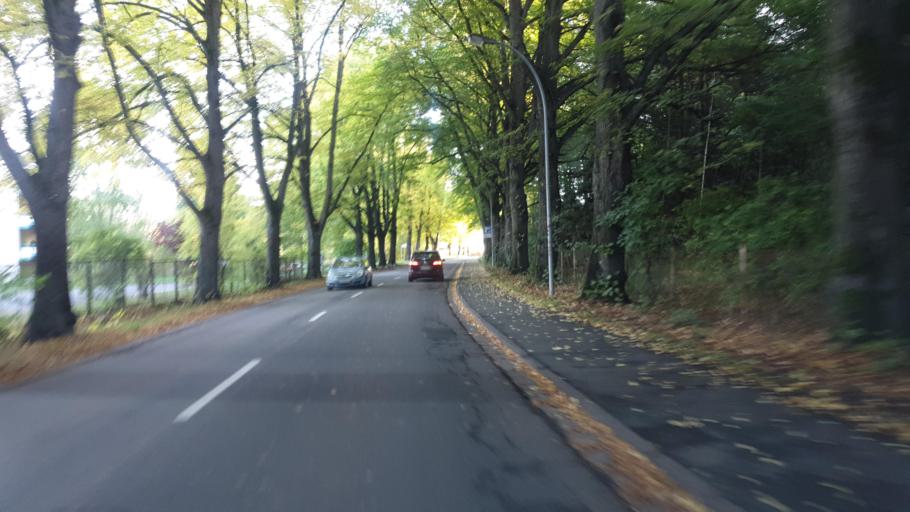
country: DE
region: Saxony
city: Chemnitz
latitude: 50.8083
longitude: 12.9502
